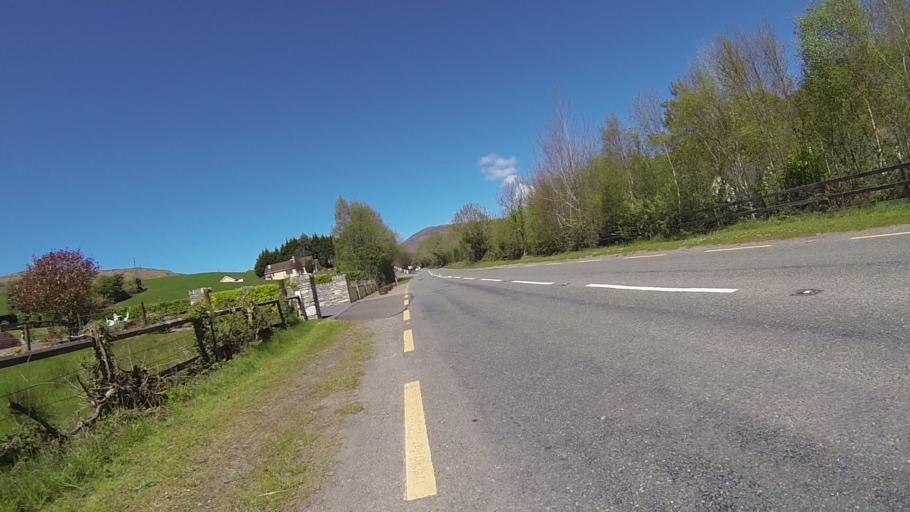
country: IE
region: Munster
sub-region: Ciarrai
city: Kenmare
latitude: 51.8912
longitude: -9.5993
